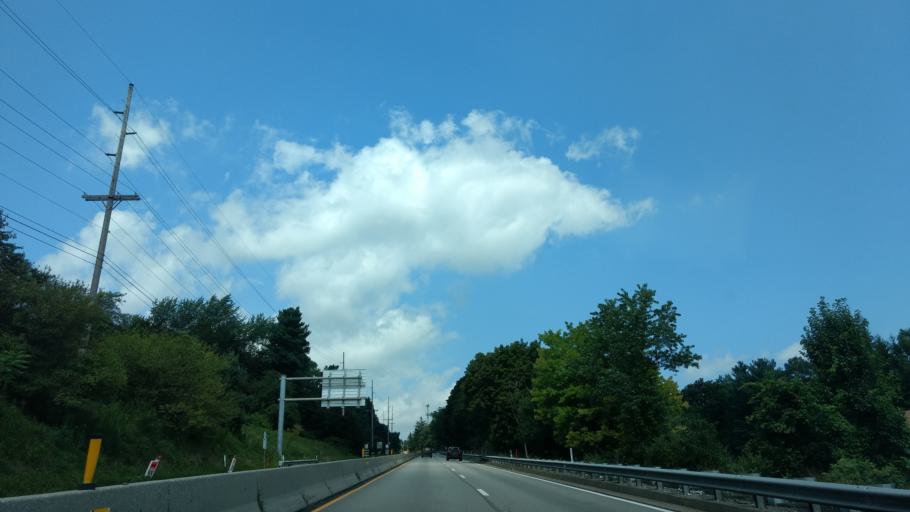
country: US
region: Pennsylvania
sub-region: Allegheny County
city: Franklin Park
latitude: 40.5942
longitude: -80.0478
